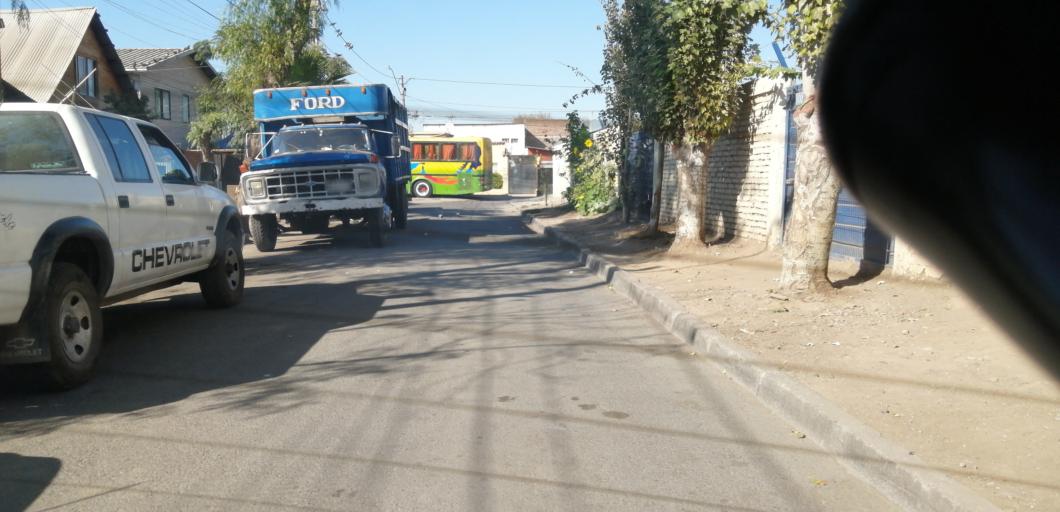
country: CL
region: Santiago Metropolitan
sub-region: Provincia de Santiago
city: Lo Prado
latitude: -33.4422
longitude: -70.7577
